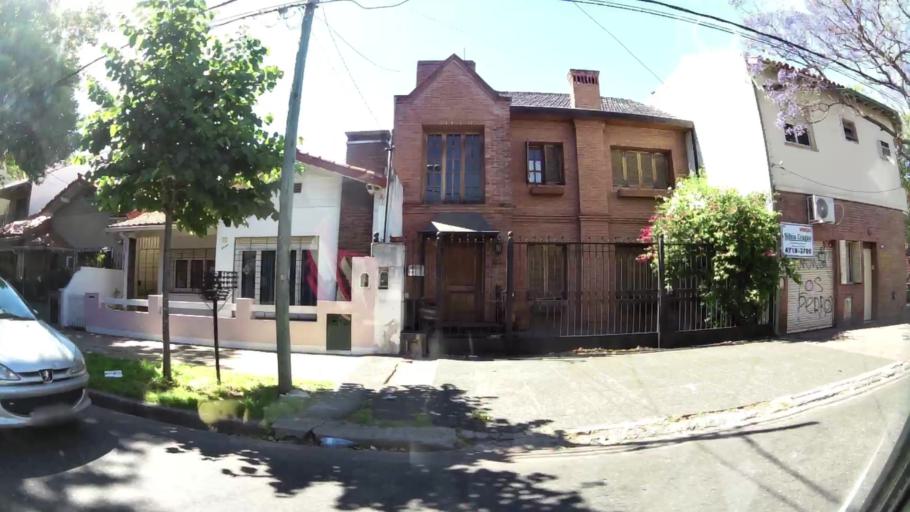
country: AR
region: Buenos Aires
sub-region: Partido de Vicente Lopez
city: Olivos
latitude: -34.5294
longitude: -58.5025
